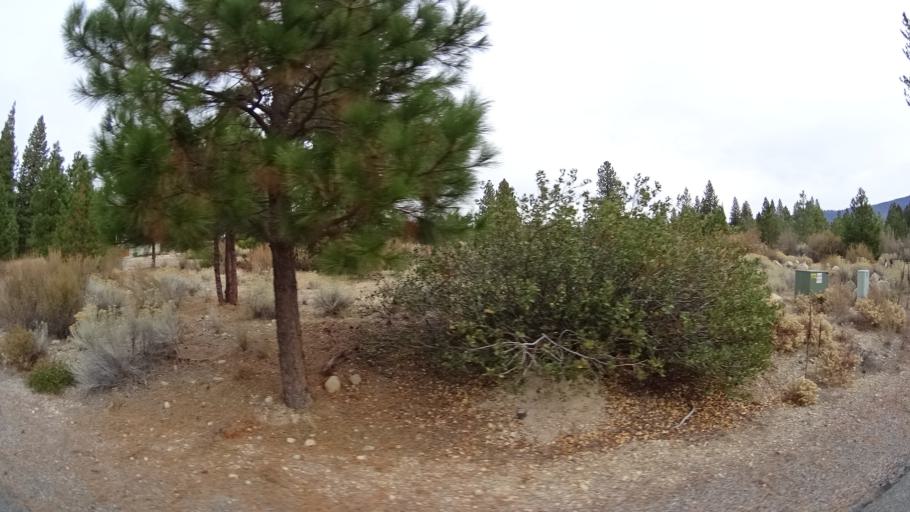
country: US
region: California
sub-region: Siskiyou County
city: Weed
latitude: 41.4129
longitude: -122.3661
